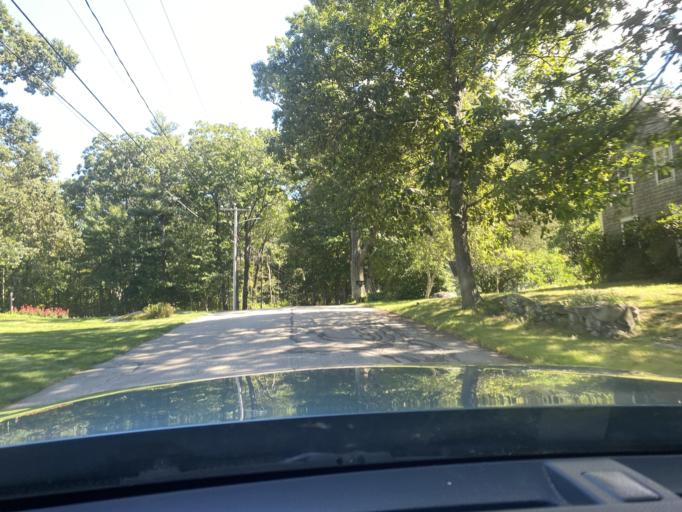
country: US
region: New Hampshire
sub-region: Rockingham County
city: Portsmouth
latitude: 43.0576
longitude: -70.7594
